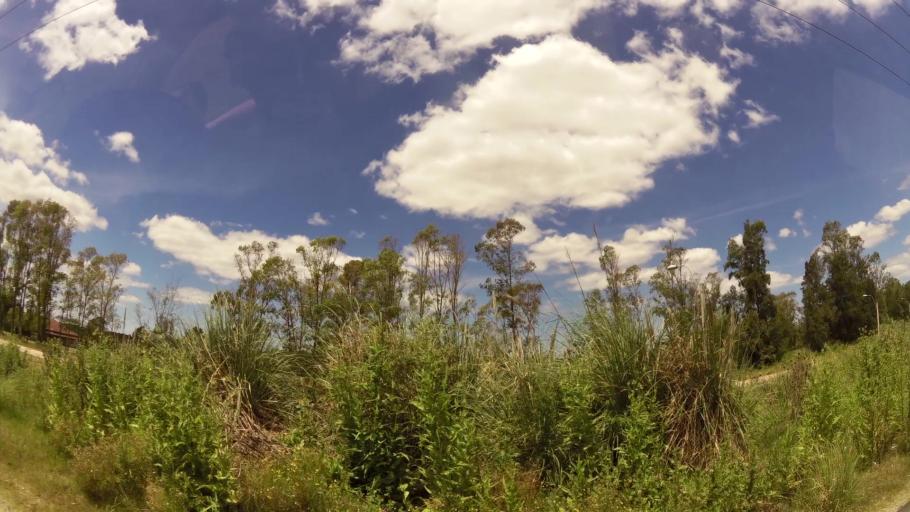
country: UY
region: Canelones
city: Colonia Nicolich
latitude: -34.8066
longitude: -55.9588
